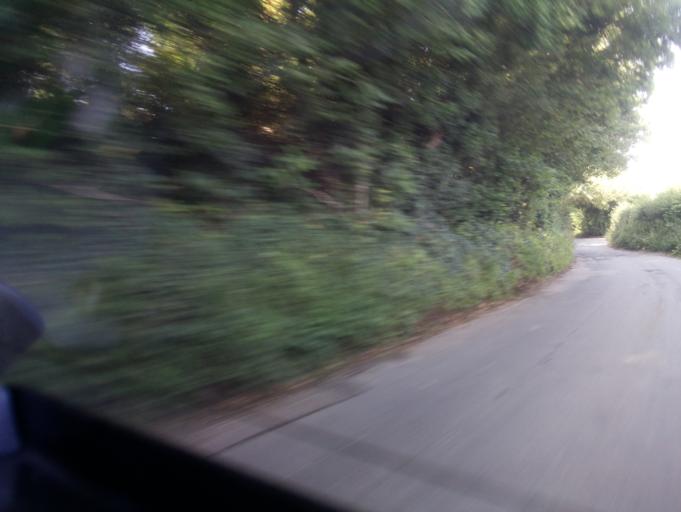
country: GB
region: England
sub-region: South Gloucestershire
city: Bitton
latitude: 51.4401
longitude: -2.4464
